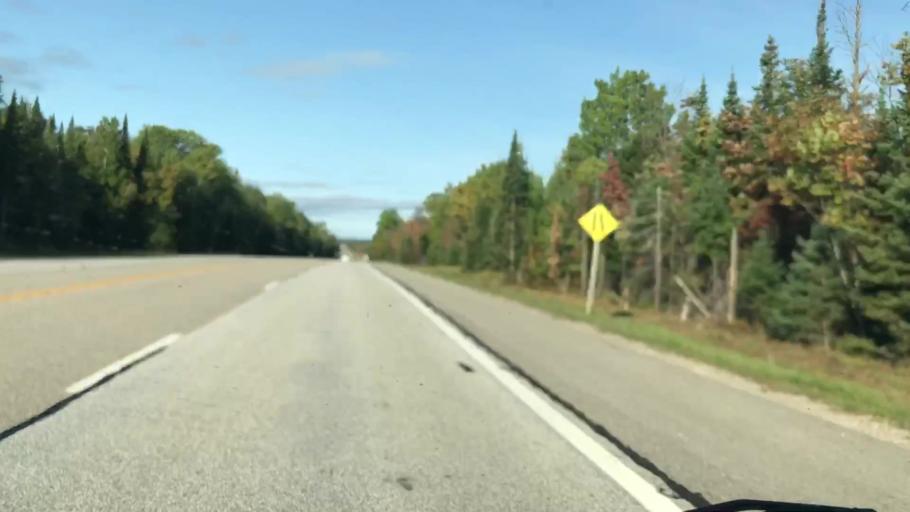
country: US
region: Michigan
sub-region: Luce County
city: Newberry
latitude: 46.3037
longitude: -85.2904
